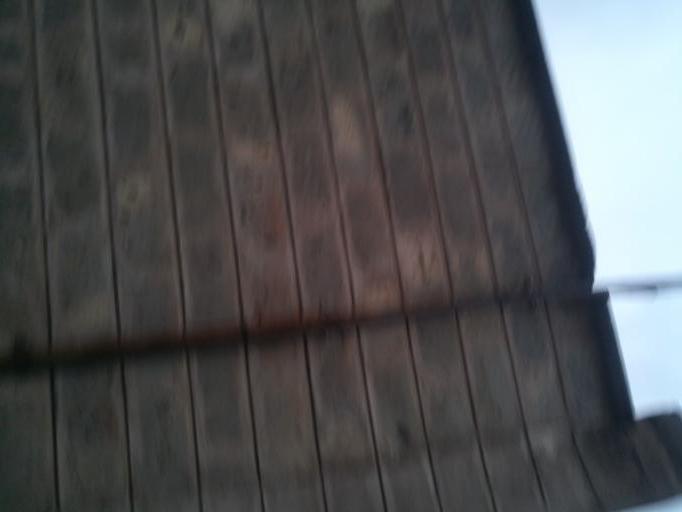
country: KE
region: Nairobi Area
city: Nairobi
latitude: -1.2975
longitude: 36.8000
